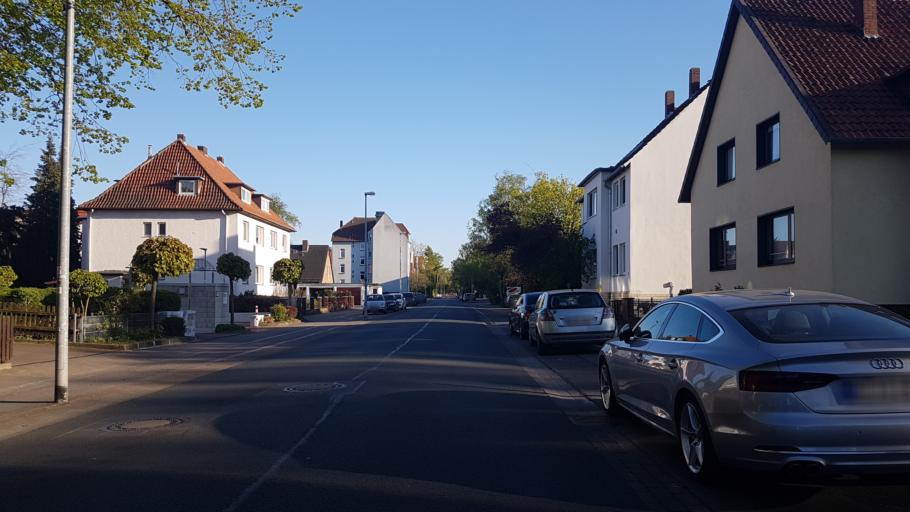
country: DE
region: Lower Saxony
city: Hannover
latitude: 52.3960
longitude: 9.8032
